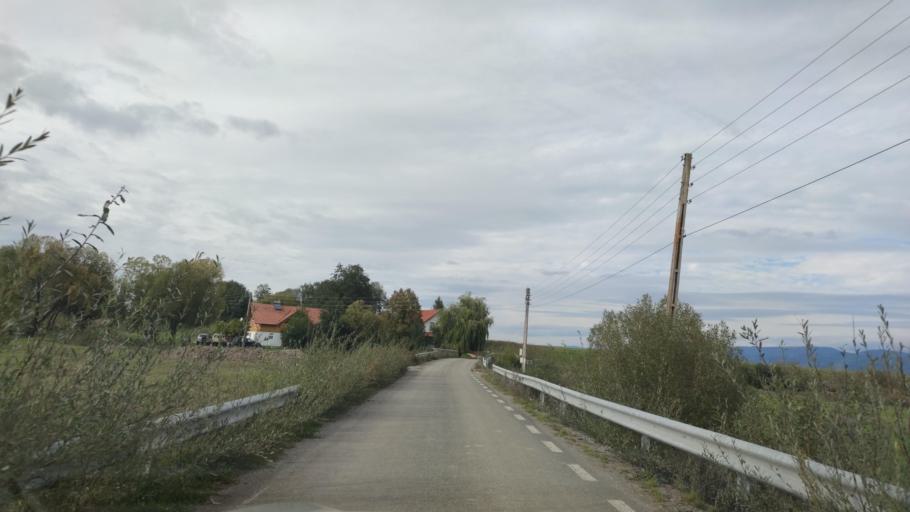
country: RO
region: Harghita
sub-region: Comuna Remetea
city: Remetea
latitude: 46.8123
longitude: 25.4226
